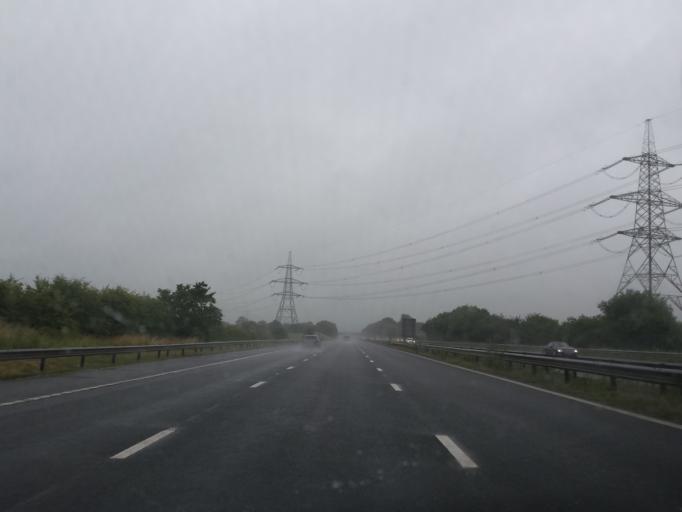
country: GB
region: England
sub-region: Leicestershire
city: Enderby
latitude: 52.5910
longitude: -1.2276
